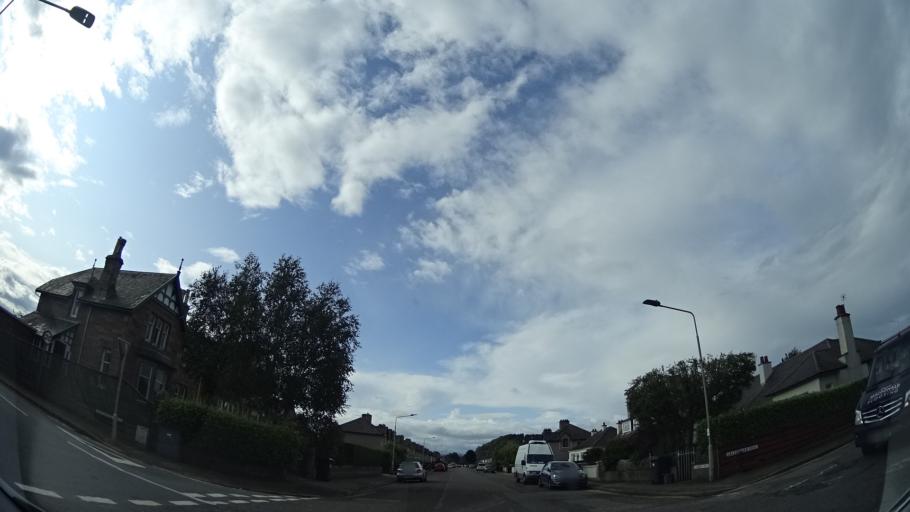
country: GB
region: Scotland
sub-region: Highland
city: Inverness
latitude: 57.4771
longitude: -4.2393
